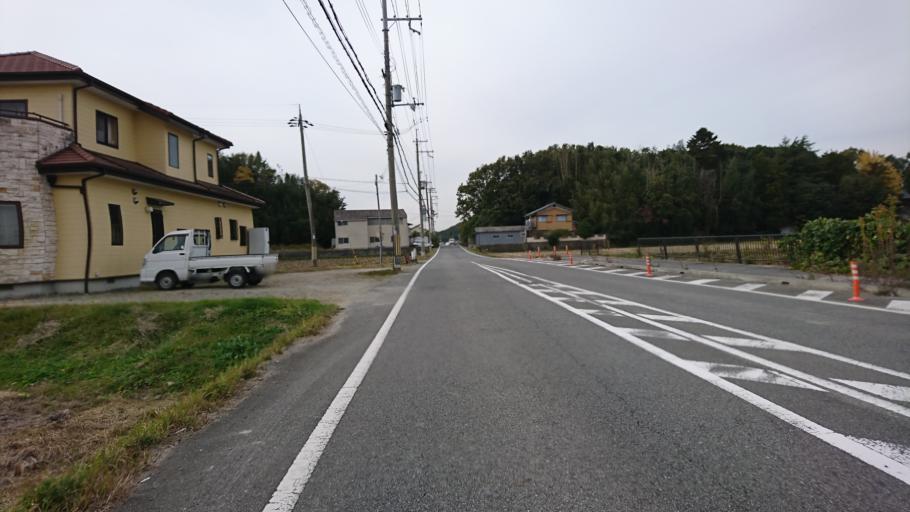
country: JP
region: Hyogo
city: Ono
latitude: 34.7864
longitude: 134.9000
